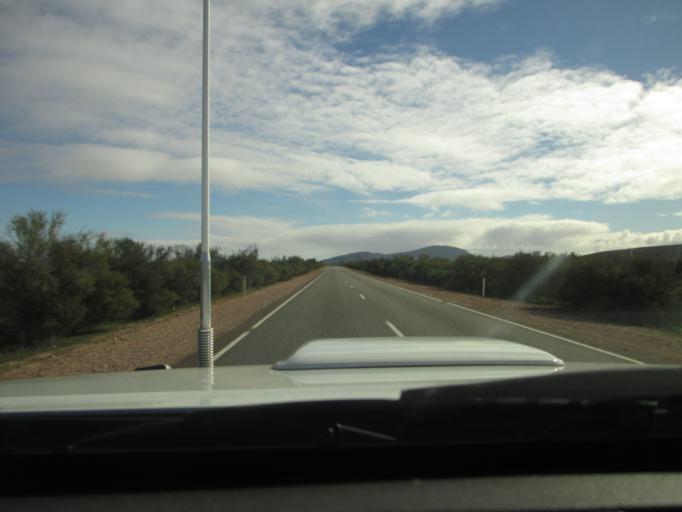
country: AU
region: South Australia
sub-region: Flinders Ranges
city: Quorn
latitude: -31.8452
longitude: 138.3936
